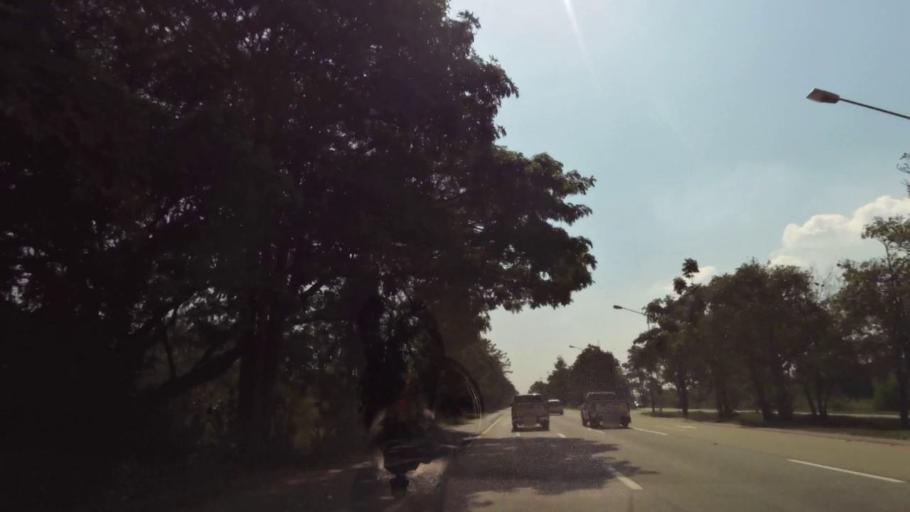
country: TH
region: Phichit
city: Wachira Barami
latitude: 16.5735
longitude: 100.1484
